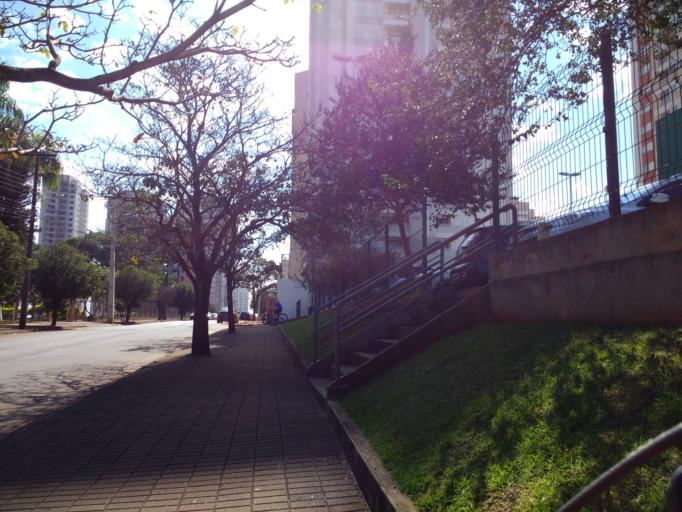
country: BR
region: Parana
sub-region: Londrina
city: Londrina
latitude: -23.3358
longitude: -51.1812
